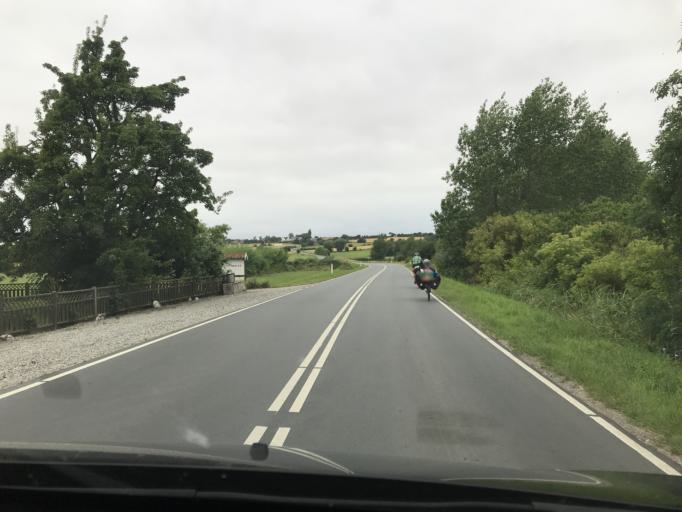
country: DK
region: South Denmark
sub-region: AEro Kommune
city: AEroskobing
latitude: 54.8387
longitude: 10.4420
